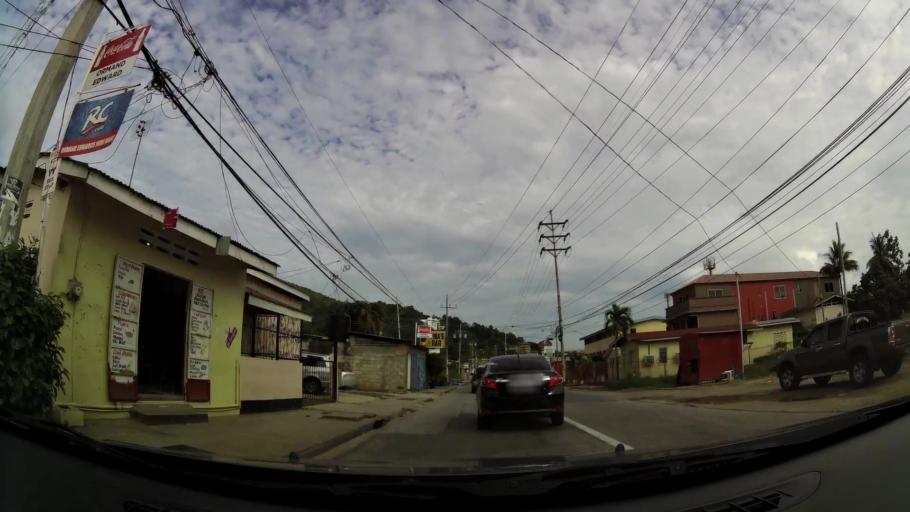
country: TT
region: City of Port of Spain
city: Mucurapo
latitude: 10.6855
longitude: -61.5955
